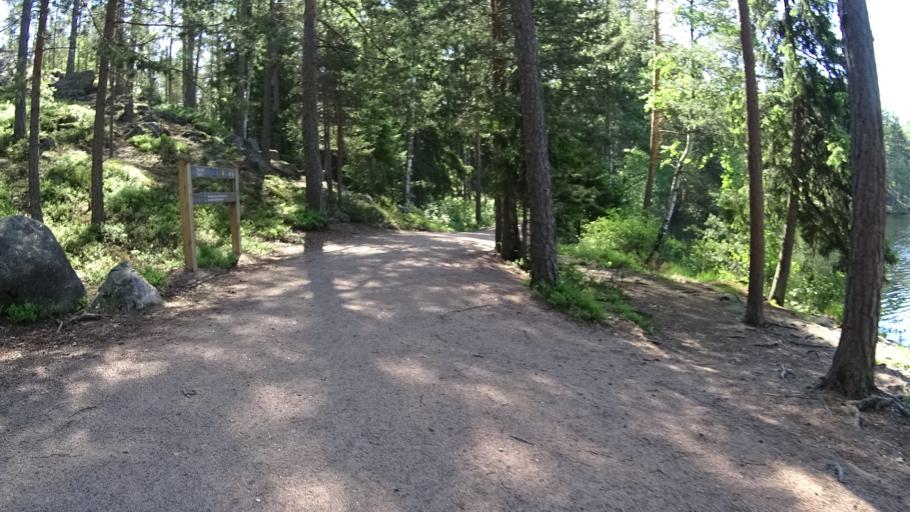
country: FI
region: Uusimaa
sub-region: Helsinki
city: Espoo
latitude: 60.3231
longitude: 24.6641
